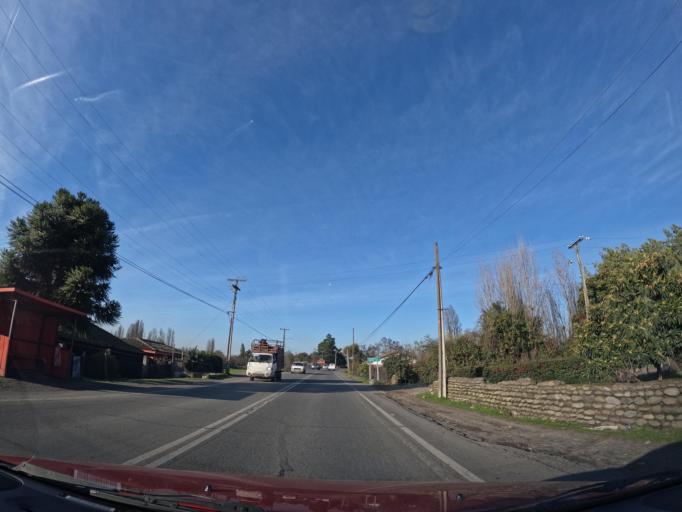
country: CL
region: Maule
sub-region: Provincia de Talca
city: San Clemente
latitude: -35.6224
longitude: -71.4921
